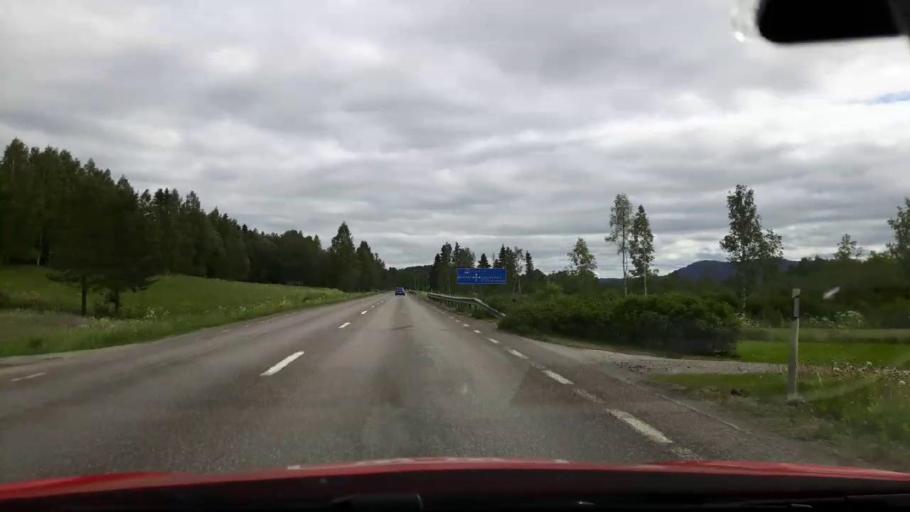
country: SE
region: Jaemtland
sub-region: Ragunda Kommun
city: Hammarstrand
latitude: 63.1224
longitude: 16.3610
